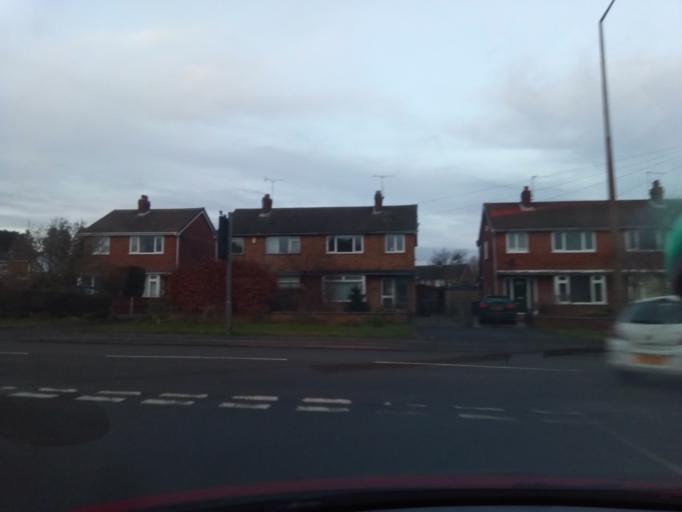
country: GB
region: England
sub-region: Derbyshire
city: Borrowash
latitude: 52.9056
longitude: -1.3779
